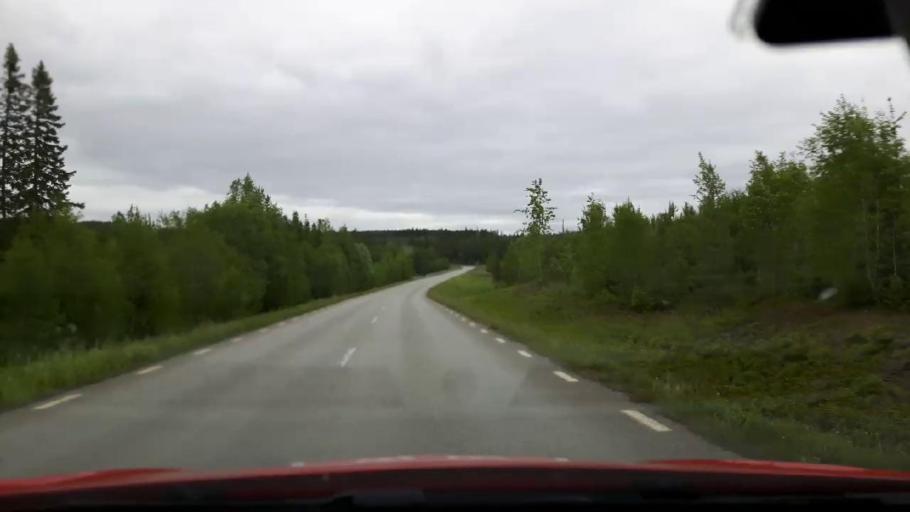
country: SE
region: Jaemtland
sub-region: OEstersunds Kommun
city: Lit
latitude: 63.6745
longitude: 14.6712
